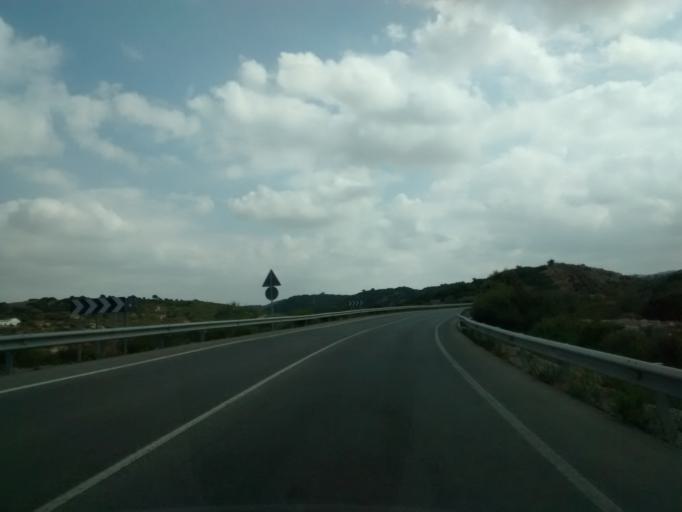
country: ES
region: Andalusia
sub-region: Provincia de Cadiz
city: Medina Sidonia
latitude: 36.4442
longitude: -6.0225
